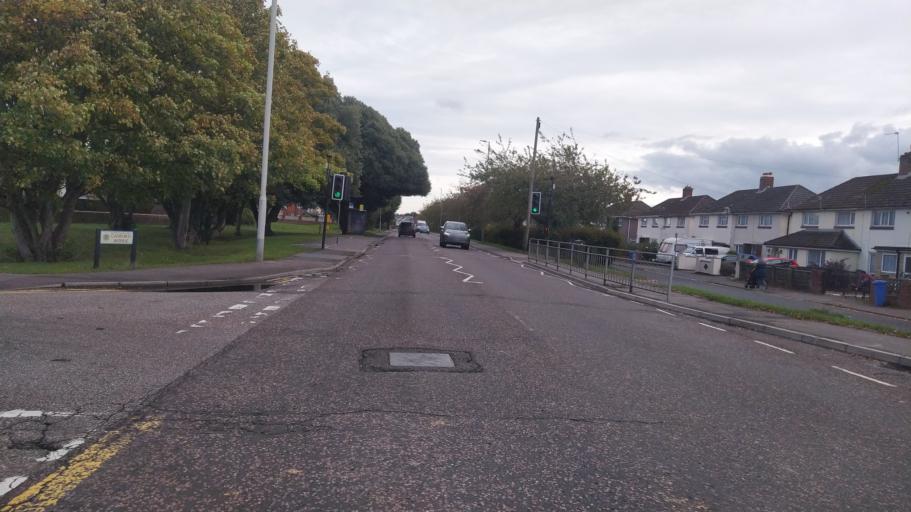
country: GB
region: England
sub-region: Dorset
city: Parkstone
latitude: 50.7494
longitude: -1.9218
